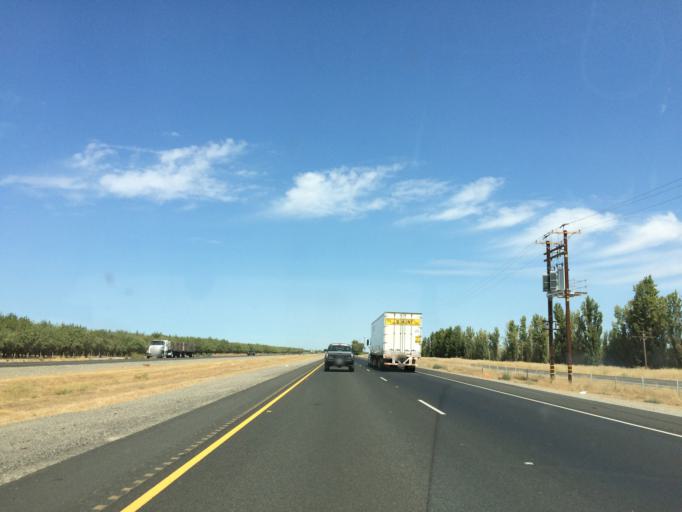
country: US
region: California
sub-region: Colusa County
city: Arbuckle
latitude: 38.9902
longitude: -122.0393
